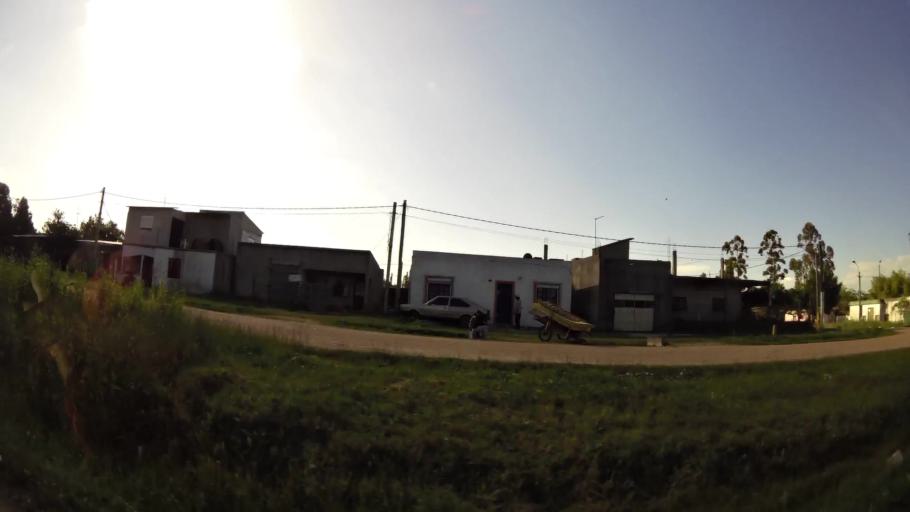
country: UY
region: Canelones
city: La Paz
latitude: -34.8190
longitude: -56.1748
